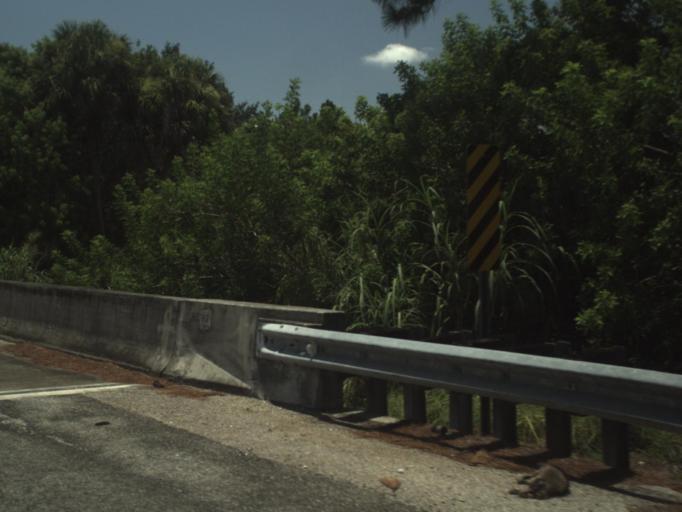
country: US
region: Florida
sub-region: Martin County
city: Indiantown
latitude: 27.0207
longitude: -80.4335
